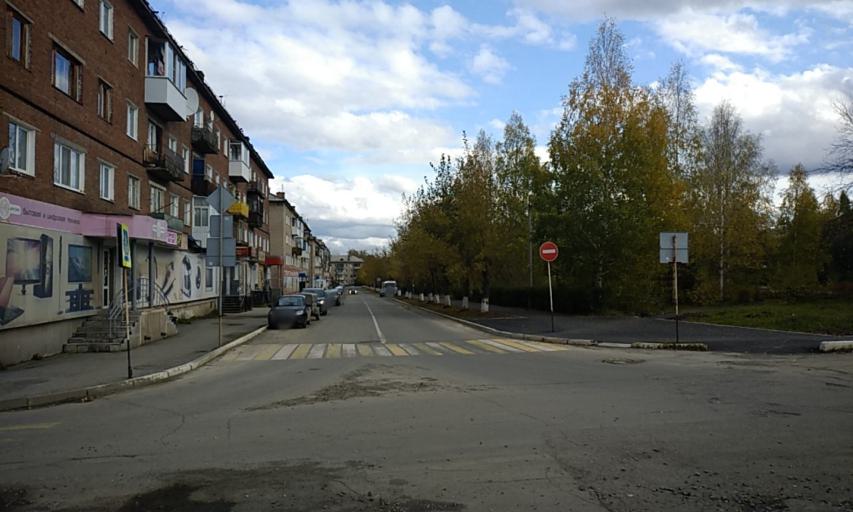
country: RU
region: Sverdlovsk
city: Krasnoural'sk
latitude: 58.3581
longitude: 60.0353
